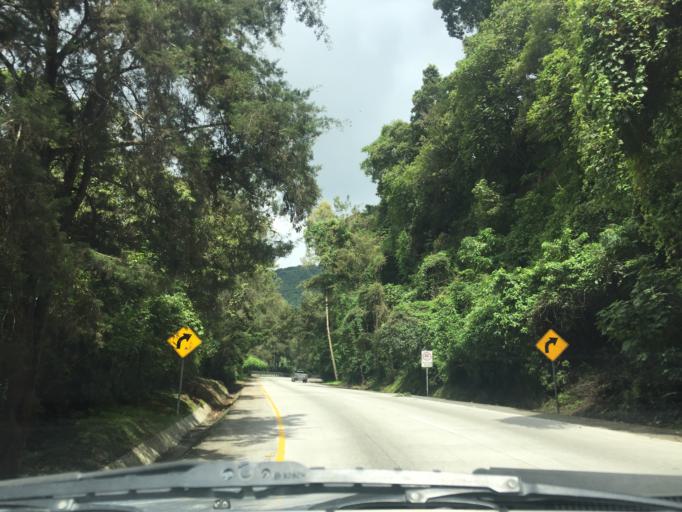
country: GT
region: Sacatepequez
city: Santa Lucia Milpas Altas
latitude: 14.5616
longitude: -90.6979
